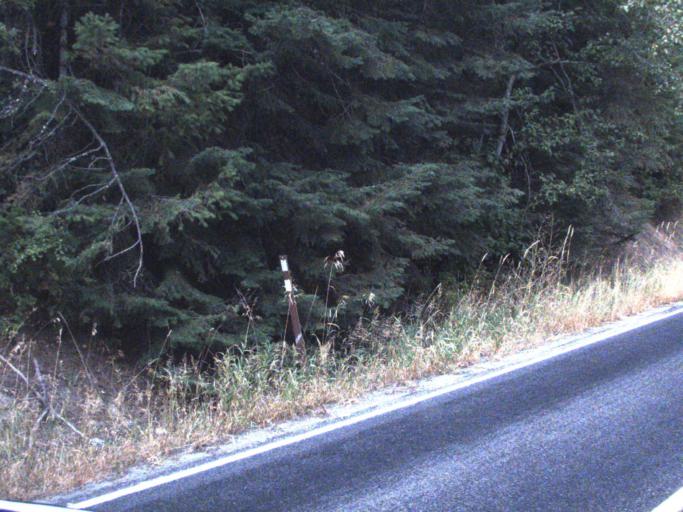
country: US
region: Washington
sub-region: Spokane County
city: Trentwood
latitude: 47.8548
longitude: -117.1639
